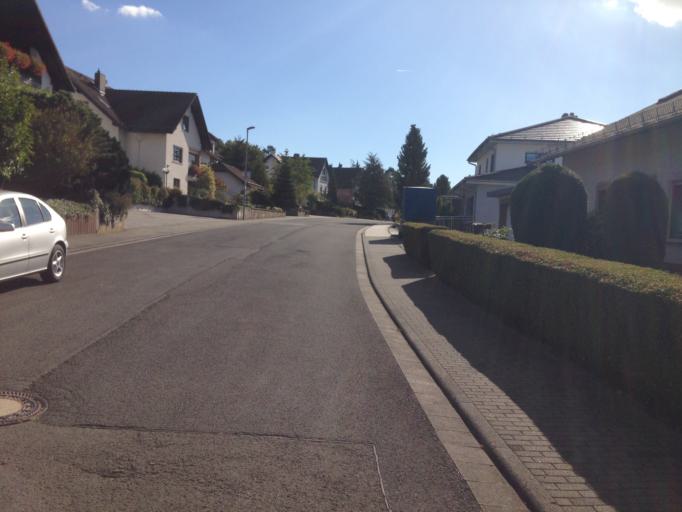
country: DE
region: Hesse
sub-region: Regierungsbezirk Giessen
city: Bad Endbach
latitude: 50.6721
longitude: 8.5335
